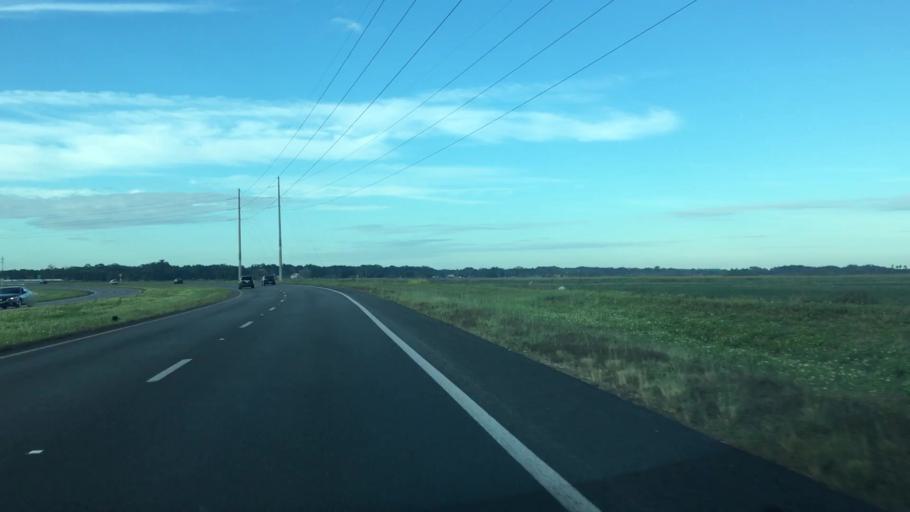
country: US
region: Florida
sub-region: Seminole County
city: Midway
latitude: 28.8076
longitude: -81.2049
